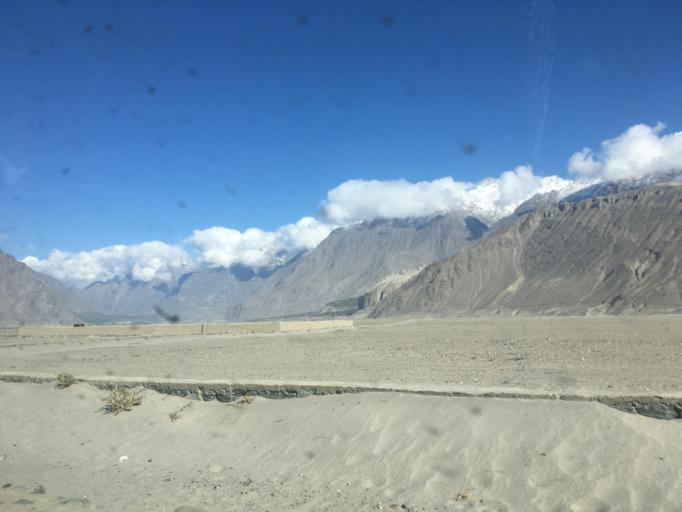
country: PK
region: Gilgit-Baltistan
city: Skardu
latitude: 35.3580
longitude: 75.5395
